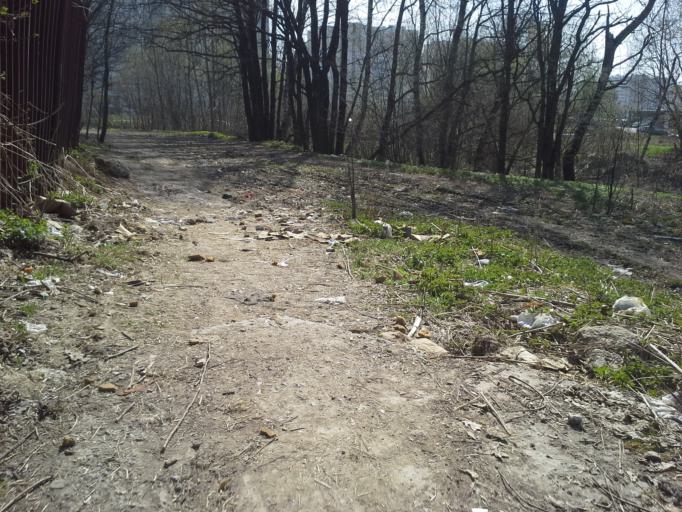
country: RU
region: Moskovskaya
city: Kommunarka
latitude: 55.5534
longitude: 37.5340
